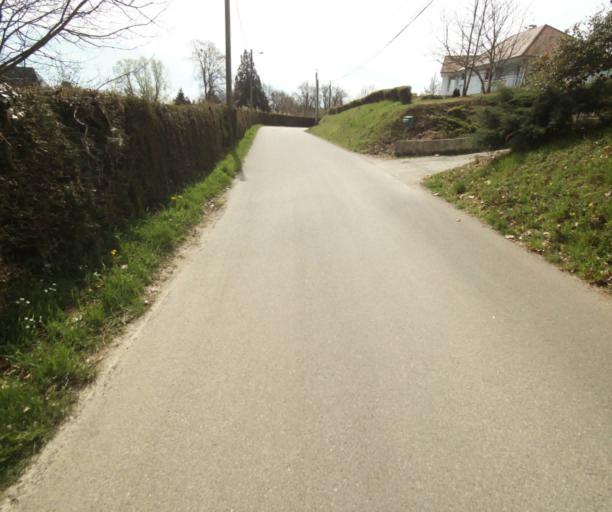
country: FR
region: Limousin
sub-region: Departement de la Correze
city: Naves
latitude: 45.3068
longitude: 1.7668
